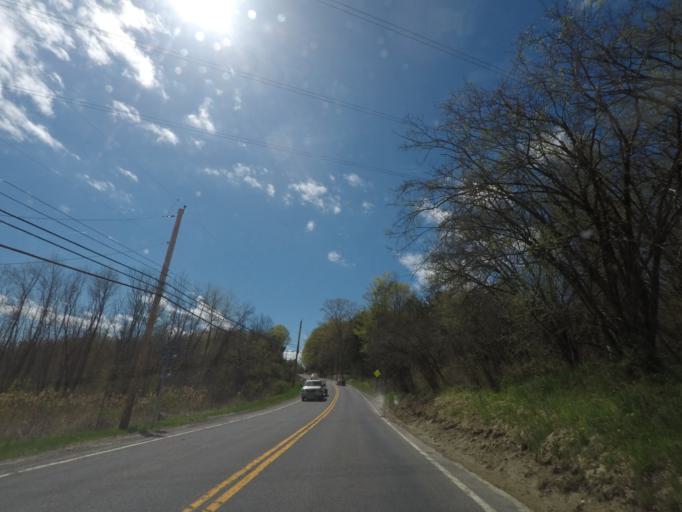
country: US
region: New York
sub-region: Greene County
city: Athens
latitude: 42.2565
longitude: -73.8241
